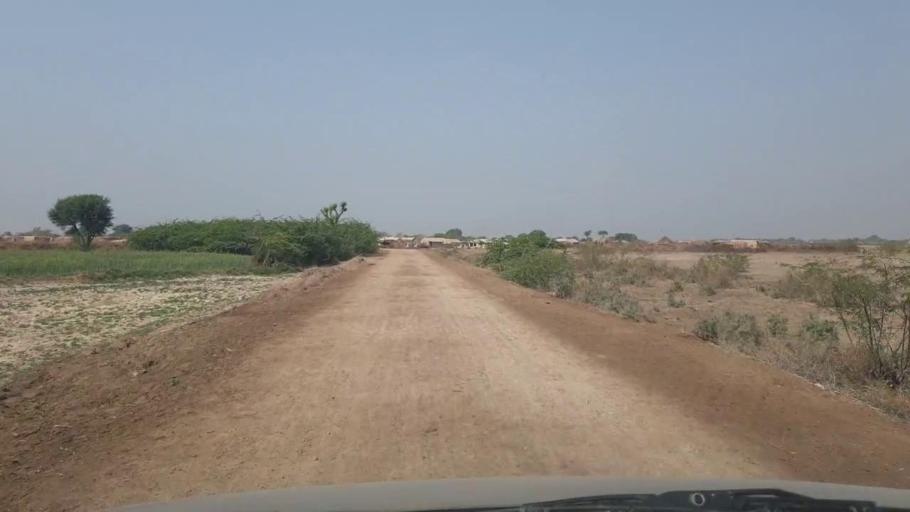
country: PK
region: Sindh
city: Chor
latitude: 25.4655
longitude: 69.7394
